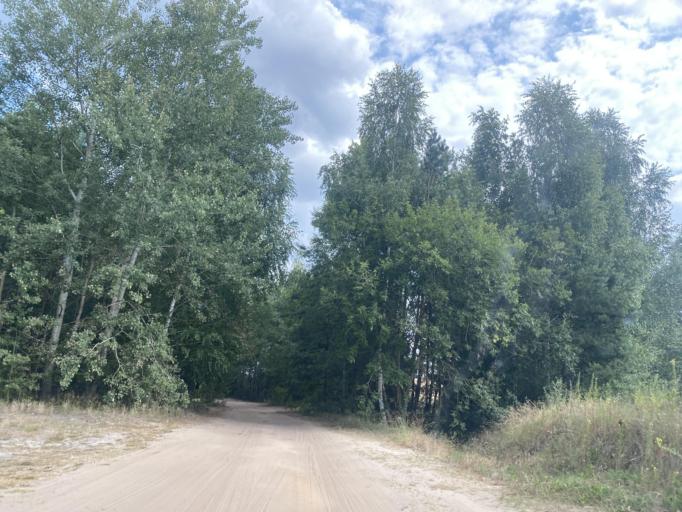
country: BY
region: Brest
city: Ivanava
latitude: 52.3661
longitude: 25.6349
